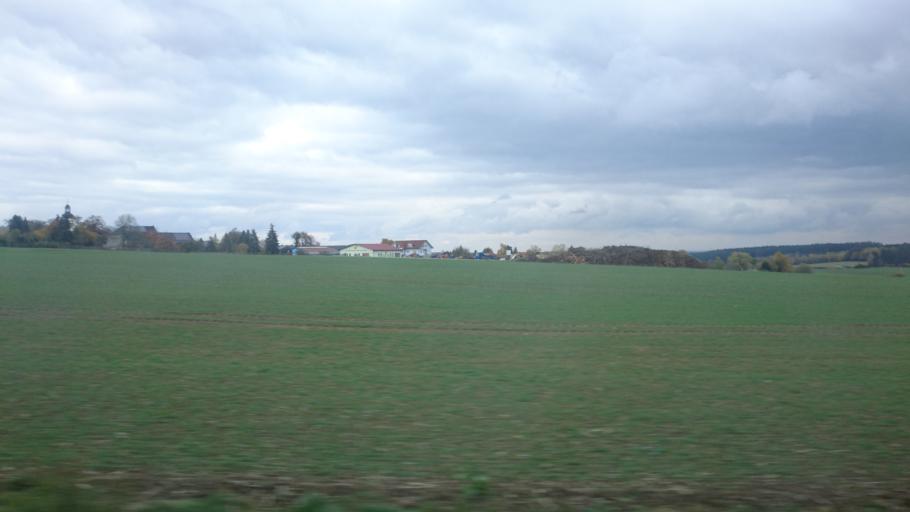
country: DE
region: Thuringia
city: Dittersdorf
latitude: 50.6397
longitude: 11.8136
